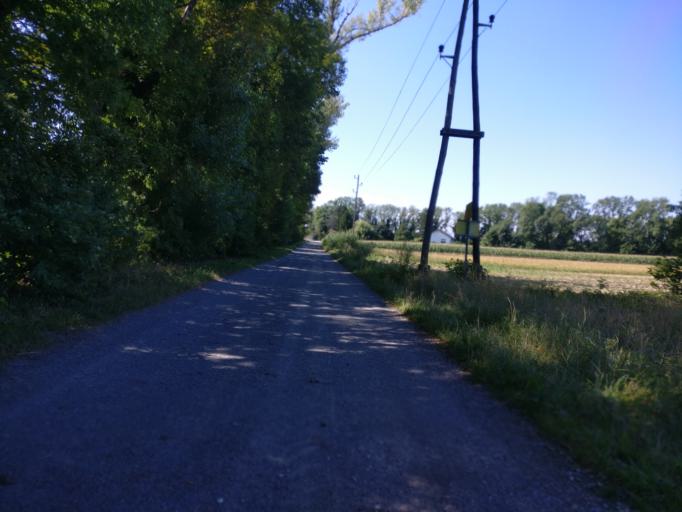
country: AT
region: Lower Austria
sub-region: Politischer Bezirk Baden
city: Pottendorf
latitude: 47.9070
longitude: 16.3522
